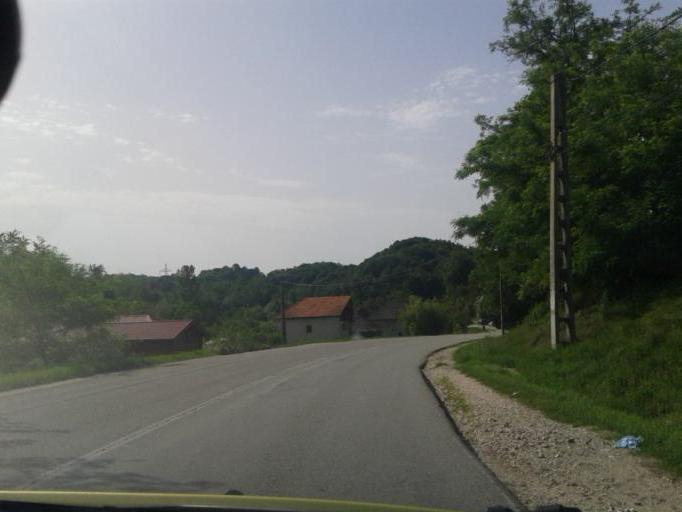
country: RO
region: Valcea
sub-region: Comuna Pietrari
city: Pietrarii de Sus
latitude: 45.1341
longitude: 24.0853
